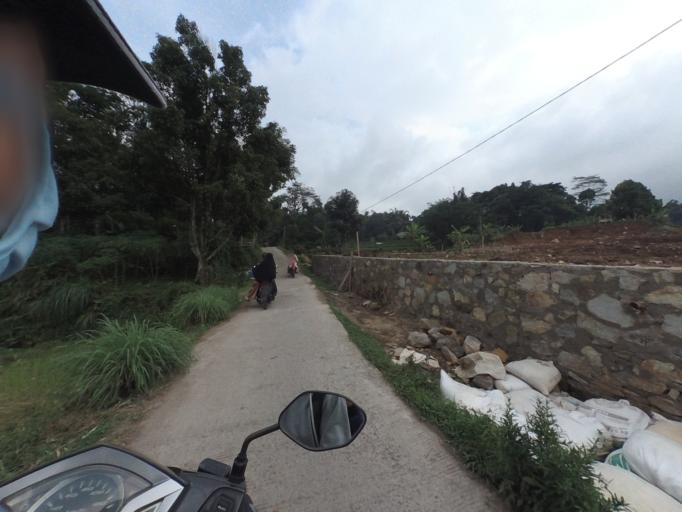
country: ID
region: West Java
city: Ciampea
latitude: -6.6876
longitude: 106.6527
